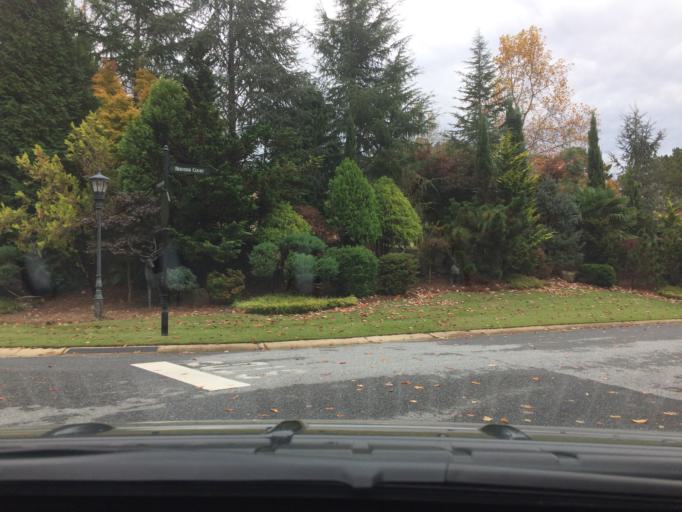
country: US
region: Georgia
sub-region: Fulton County
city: Johns Creek
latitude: 34.0089
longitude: -84.2352
